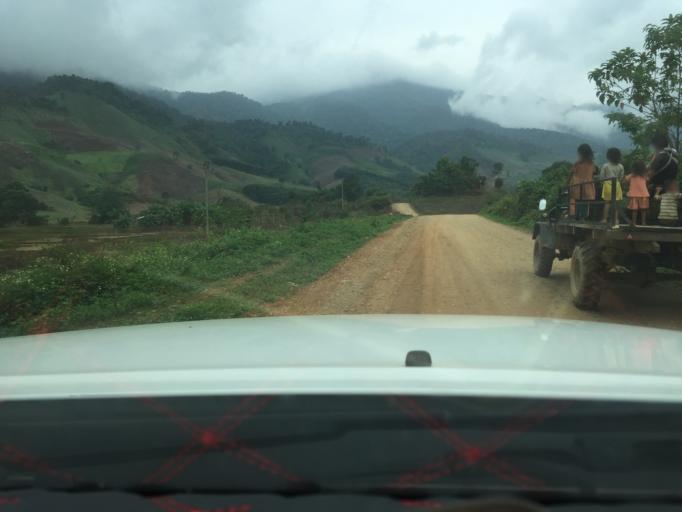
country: TH
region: Phayao
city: Phu Sang
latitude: 19.7419
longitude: 100.4428
